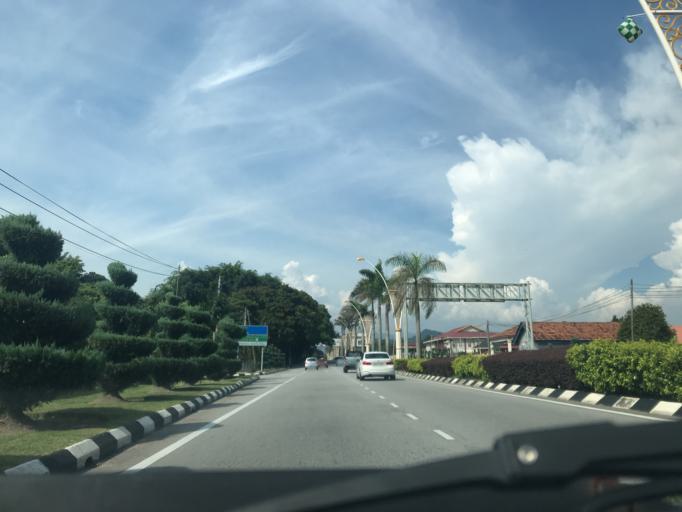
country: MY
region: Perak
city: Ipoh
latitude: 4.5926
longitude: 101.0917
